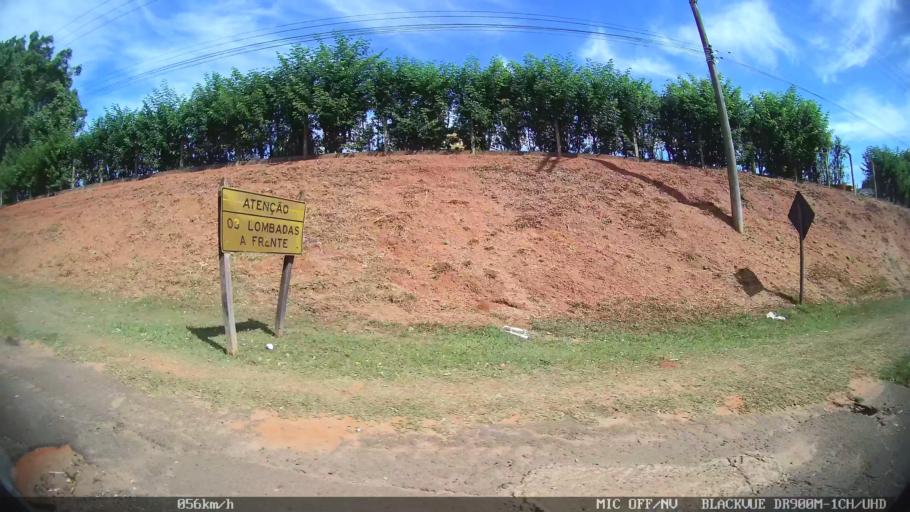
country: BR
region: Sao Paulo
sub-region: Sao Jose Do Rio Preto
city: Sao Jose do Rio Preto
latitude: -20.8298
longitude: -49.3421
